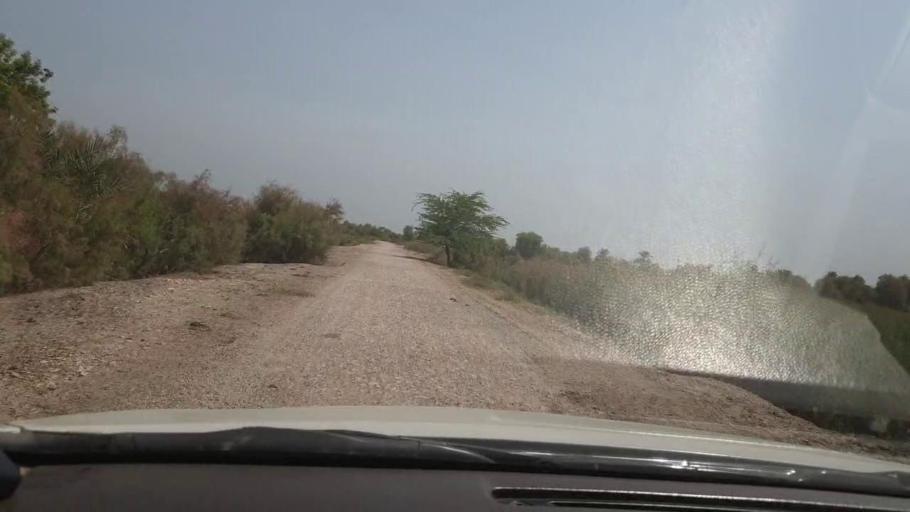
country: PK
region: Sindh
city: Shikarpur
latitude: 27.9284
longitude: 68.6045
